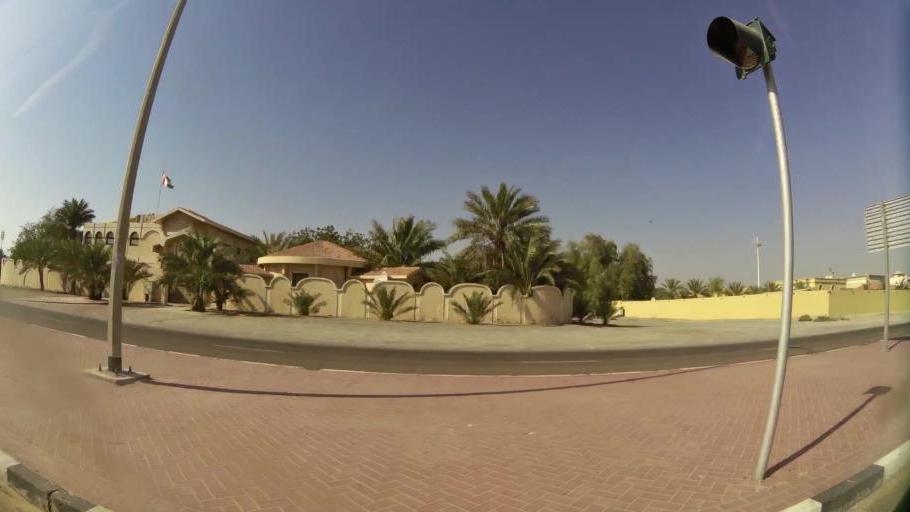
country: AE
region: Ajman
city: Ajman
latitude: 25.4078
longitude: 55.4700
